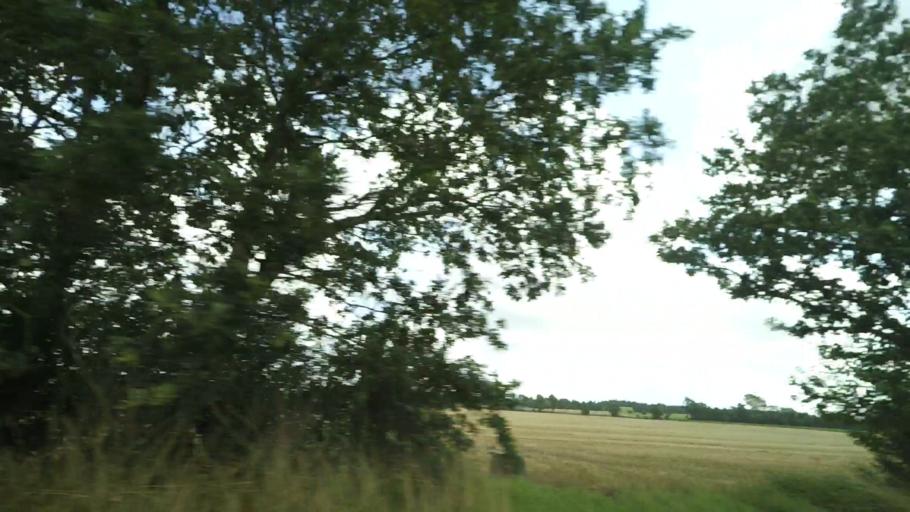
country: DK
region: Central Jutland
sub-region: Norddjurs Kommune
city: Auning
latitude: 56.5014
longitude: 10.4298
